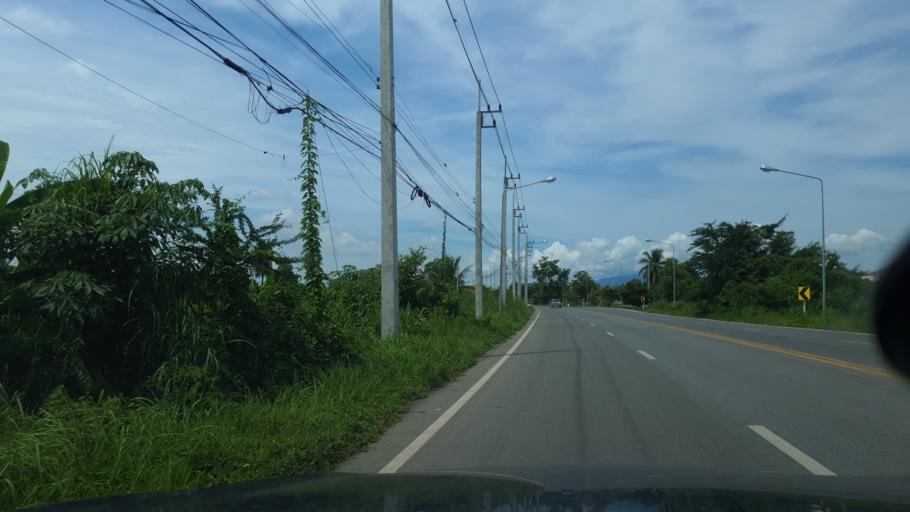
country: TH
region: Sukhothai
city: Sukhothai
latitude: 17.0509
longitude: 99.8177
